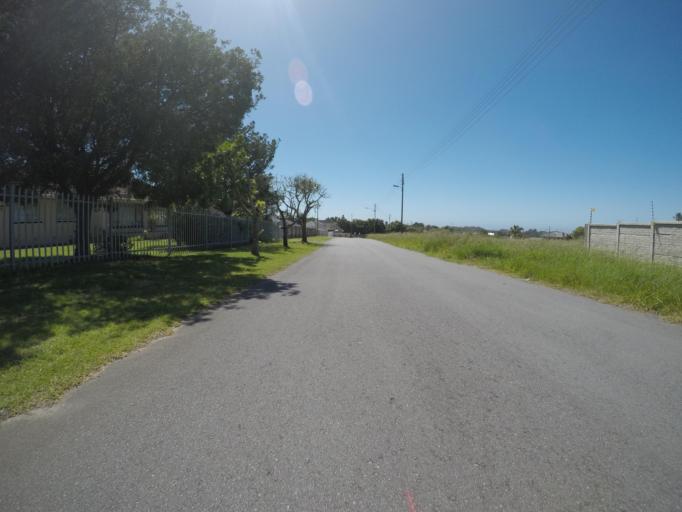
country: ZA
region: Eastern Cape
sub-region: Buffalo City Metropolitan Municipality
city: East London
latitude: -32.9685
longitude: 27.9439
